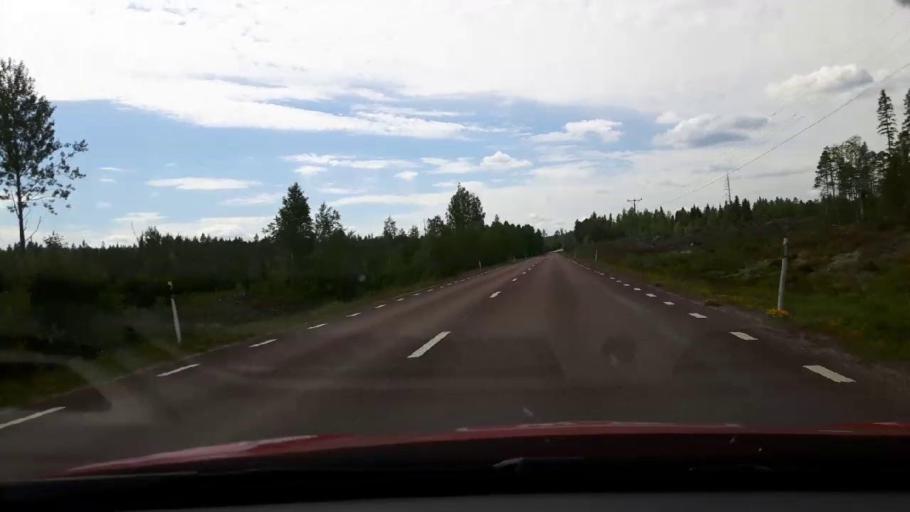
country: SE
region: Jaemtland
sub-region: Harjedalens Kommun
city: Sveg
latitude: 62.0575
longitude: 14.9073
